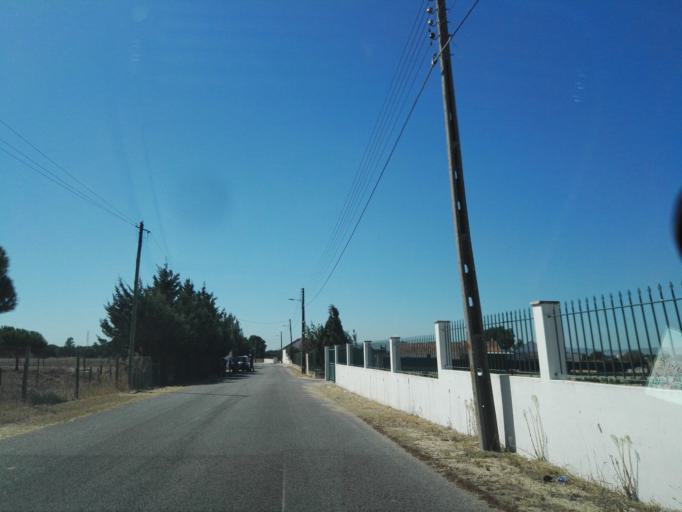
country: PT
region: Santarem
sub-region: Benavente
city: Samora Correia
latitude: 38.9065
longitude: -8.8581
